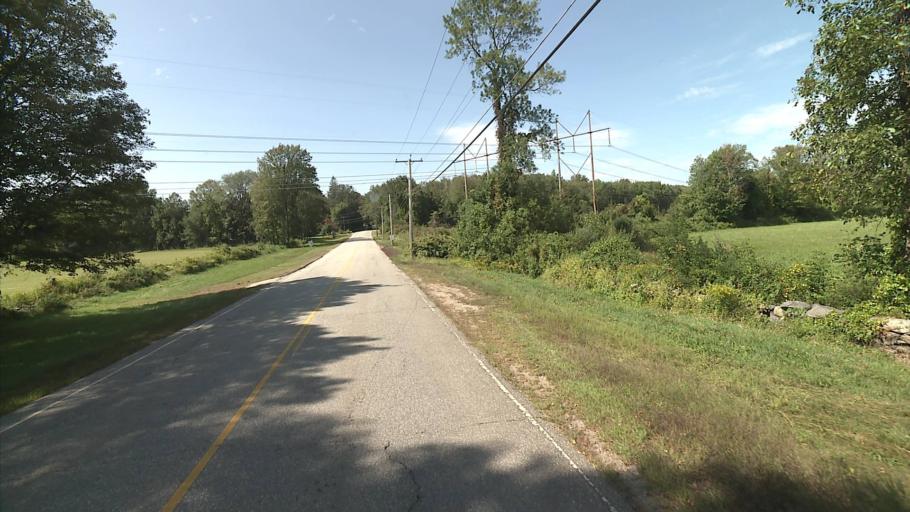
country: US
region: Connecticut
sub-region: Windham County
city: Willimantic
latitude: 41.6475
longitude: -72.2335
